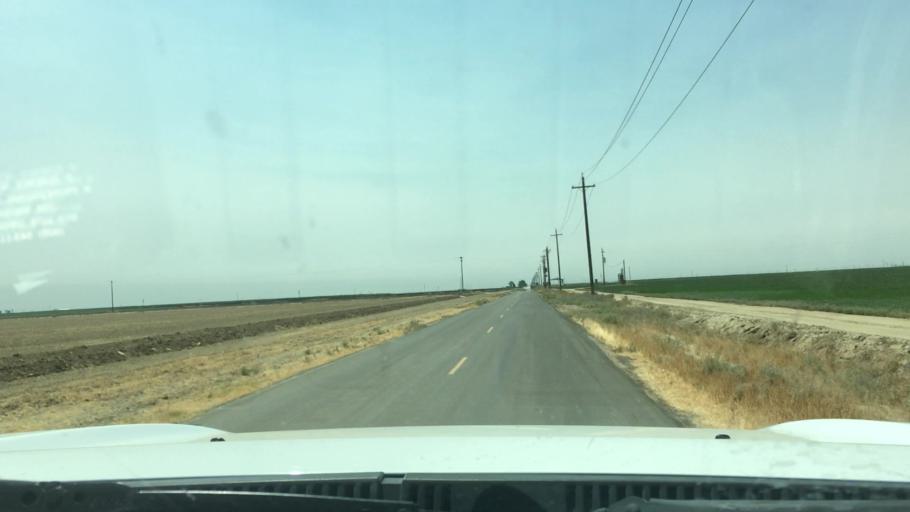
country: US
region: California
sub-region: Tulare County
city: Alpaugh
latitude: 35.7562
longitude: -119.4369
